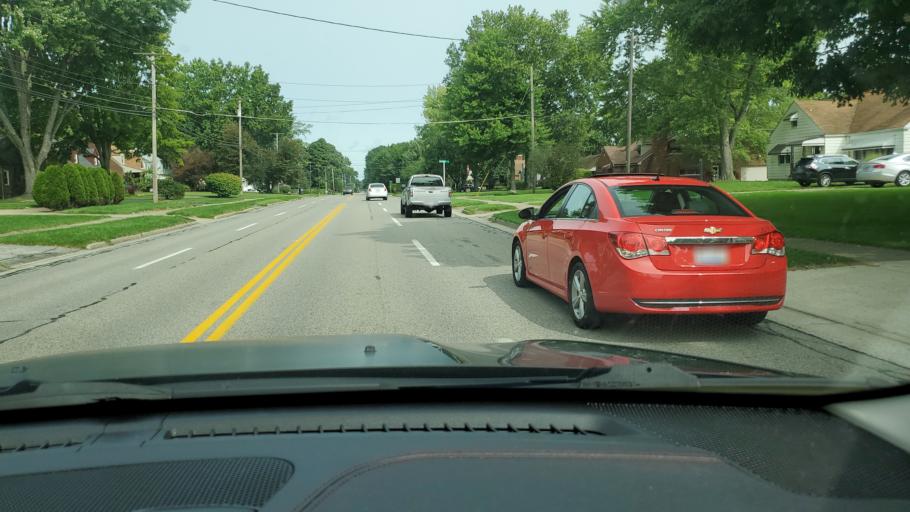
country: US
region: Ohio
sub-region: Mahoning County
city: Boardman
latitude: 41.0291
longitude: -80.6723
